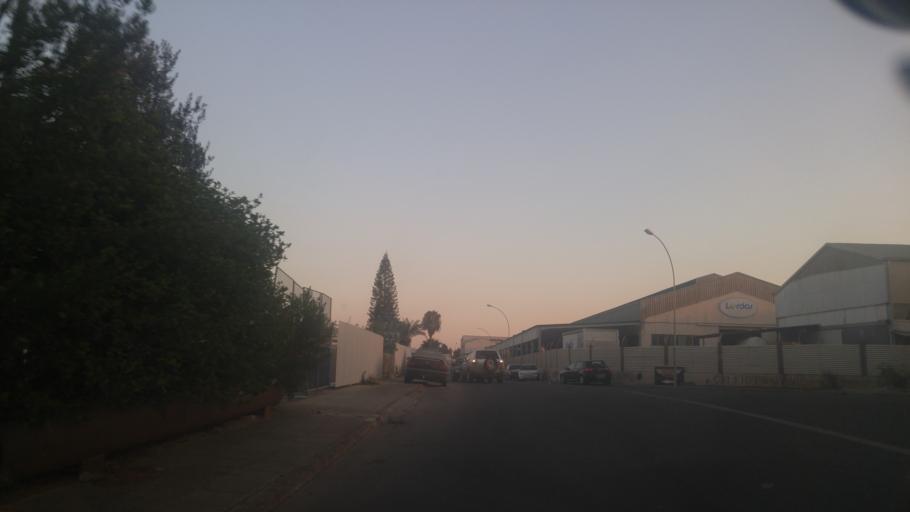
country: CY
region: Limassol
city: Pano Polemidia
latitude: 34.6679
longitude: 32.9940
